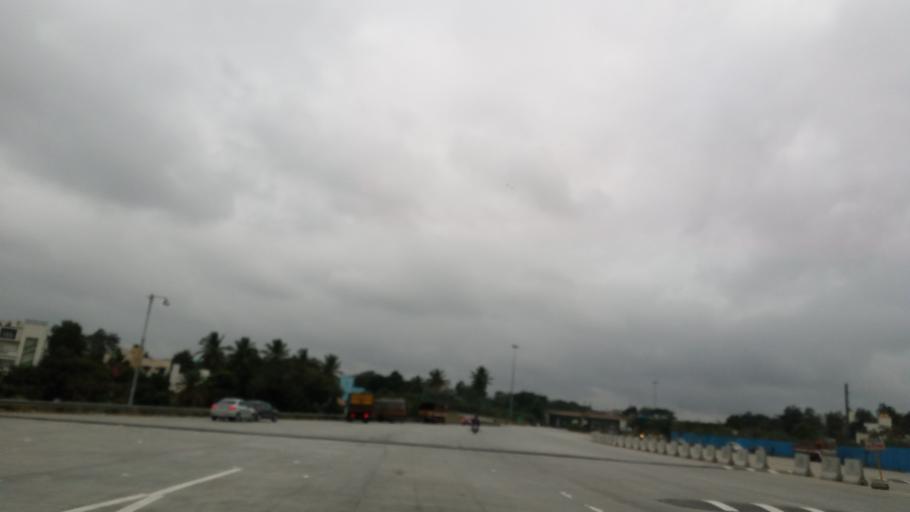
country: IN
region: Karnataka
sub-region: Bangalore Urban
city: Bangalore
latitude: 12.9367
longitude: 77.5311
